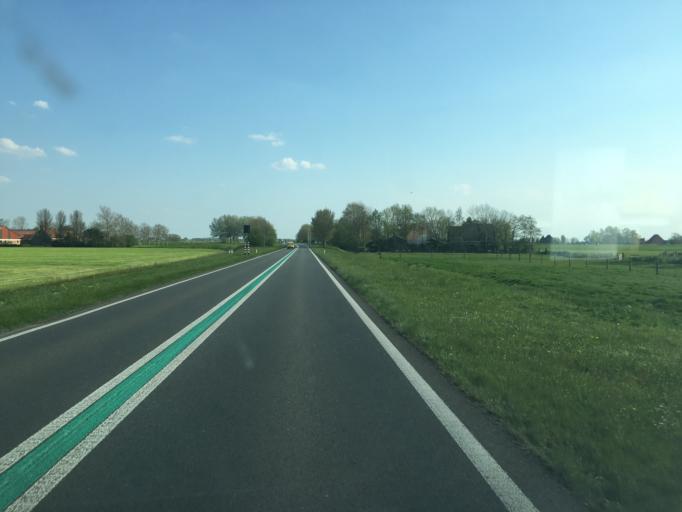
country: NL
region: Friesland
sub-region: Sudwest Fryslan
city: Workum
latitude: 52.9516
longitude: 5.4327
